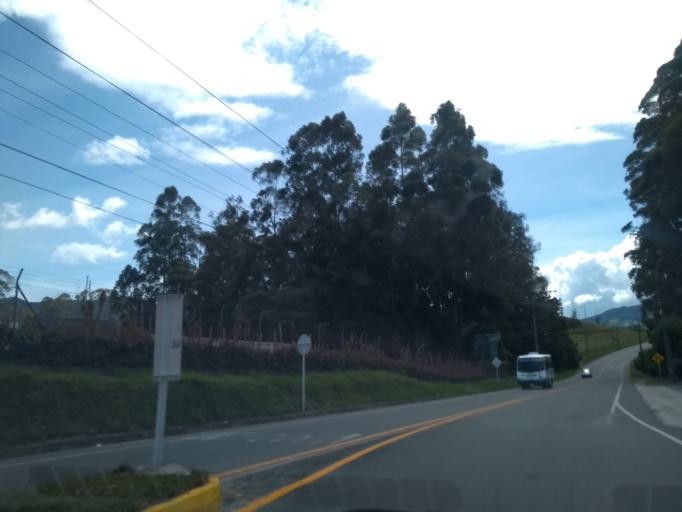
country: CO
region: Antioquia
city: Carmen de Viboral
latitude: 6.0722
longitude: -75.3799
